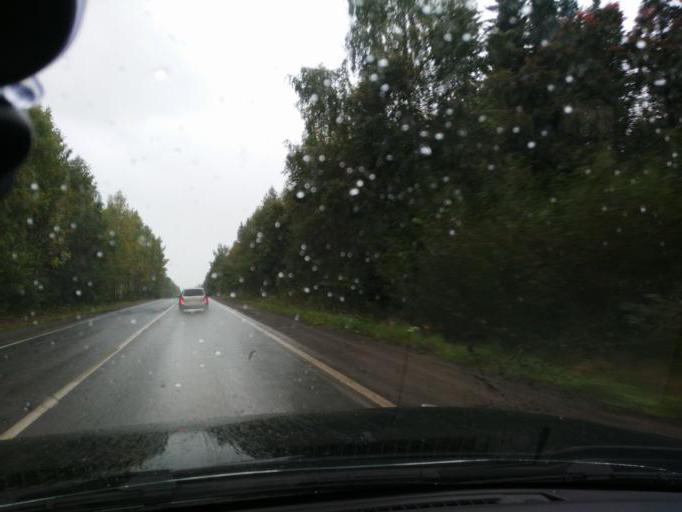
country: RU
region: Perm
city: Barda
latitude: 56.8960
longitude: 55.7297
